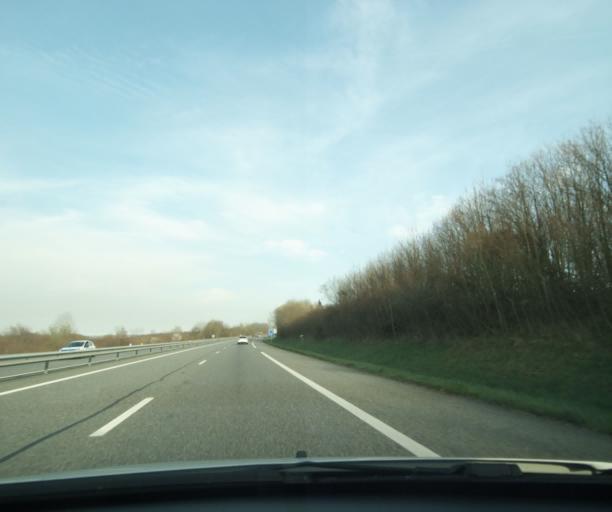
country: FR
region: Midi-Pyrenees
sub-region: Departement de la Haute-Garonne
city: Montrejeau
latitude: 43.0973
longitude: 0.5611
